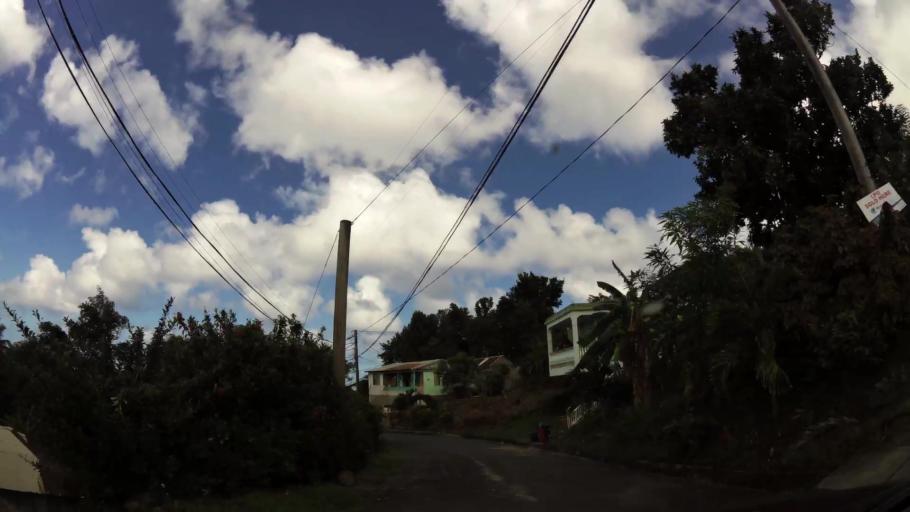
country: DM
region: Saint John
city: Portsmouth
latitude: 15.6239
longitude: -61.4641
